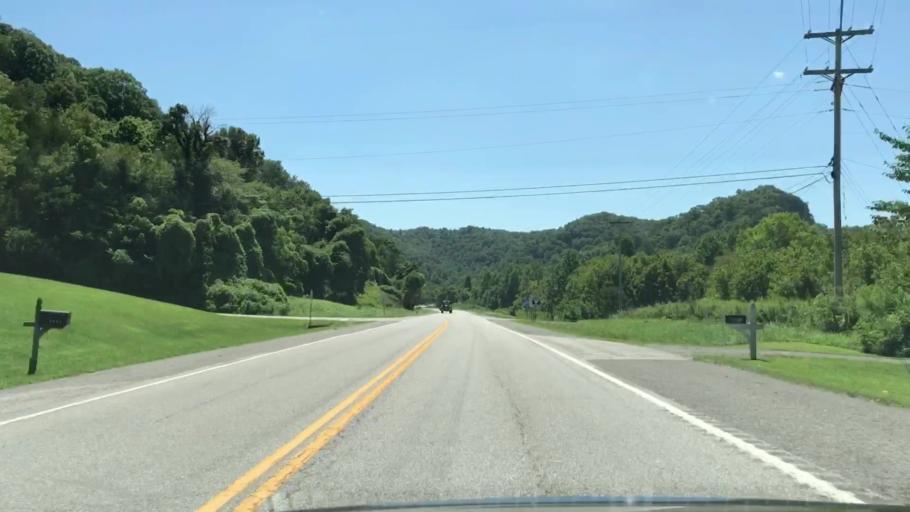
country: US
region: Tennessee
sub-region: Clay County
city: Celina
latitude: 36.4905
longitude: -85.5620
